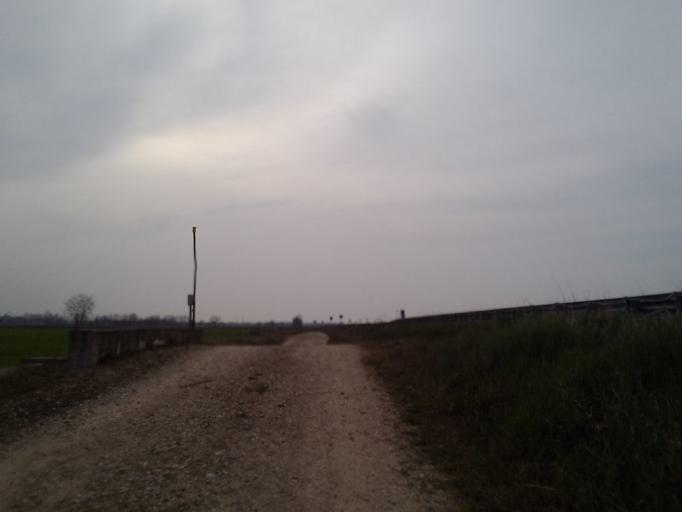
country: IT
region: Veneto
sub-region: Provincia di Verona
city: Povegliano Veronese
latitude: 45.3614
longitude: 10.8797
